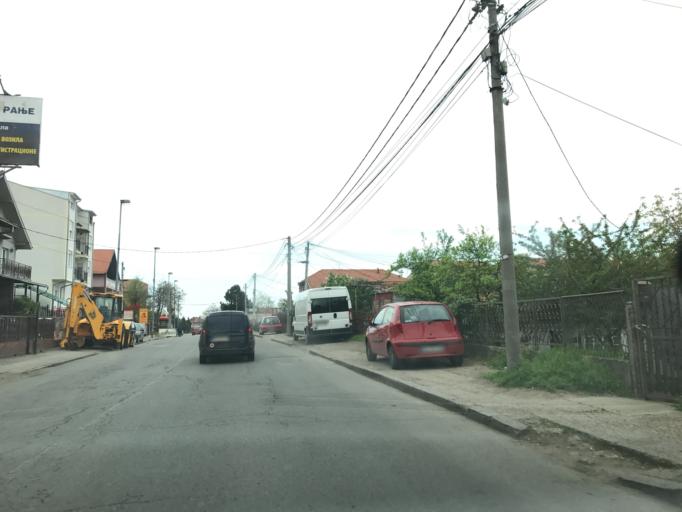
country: RS
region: Central Serbia
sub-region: Belgrade
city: Palilula
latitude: 44.8026
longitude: 20.5192
